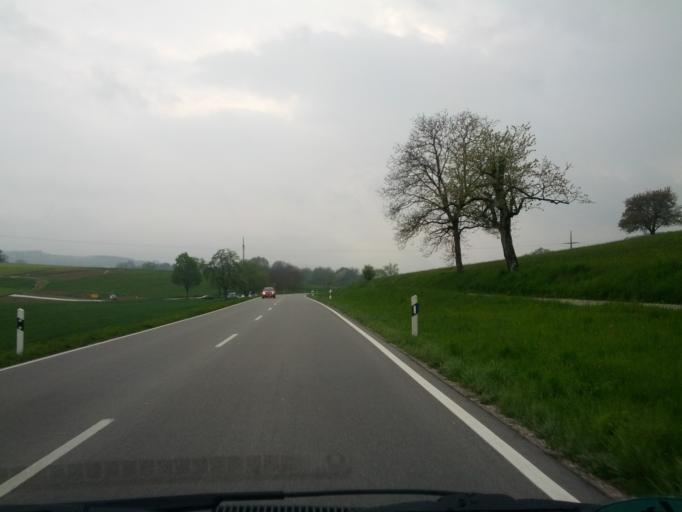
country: DE
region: Baden-Wuerttemberg
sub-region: Freiburg Region
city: Schopfheim
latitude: 47.6476
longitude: 7.8589
